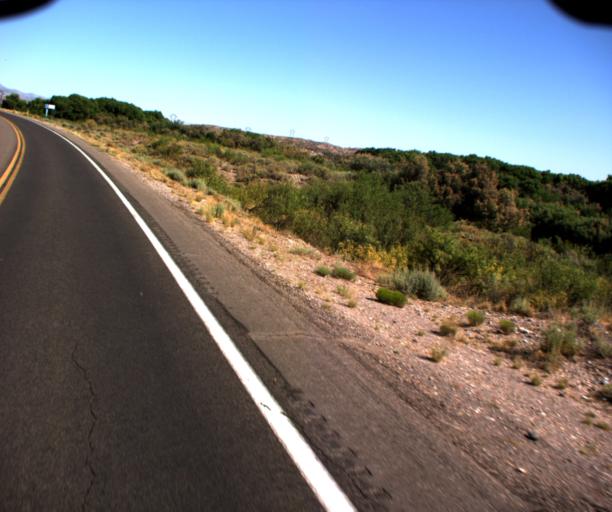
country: US
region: Arizona
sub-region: Greenlee County
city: Clifton
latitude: 32.7401
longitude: -109.1267
